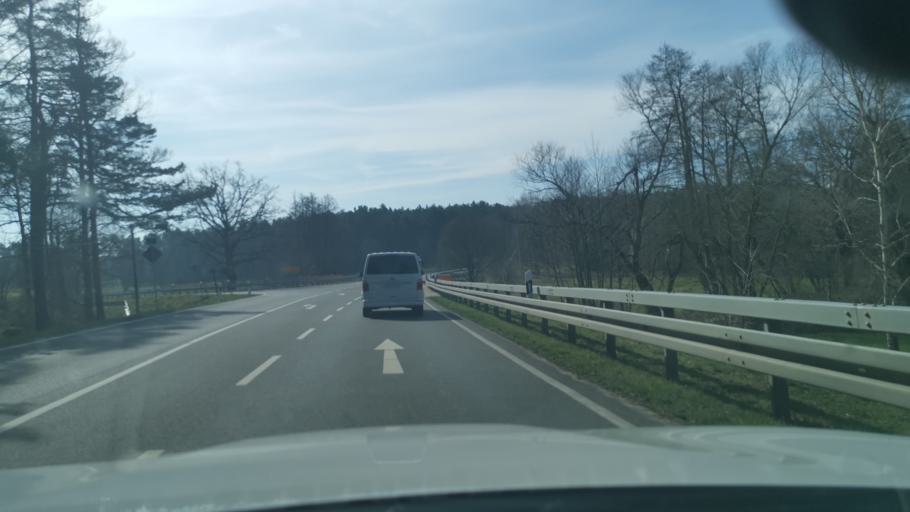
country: DE
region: Saxony-Anhalt
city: Kemberg
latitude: 51.7454
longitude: 12.6293
